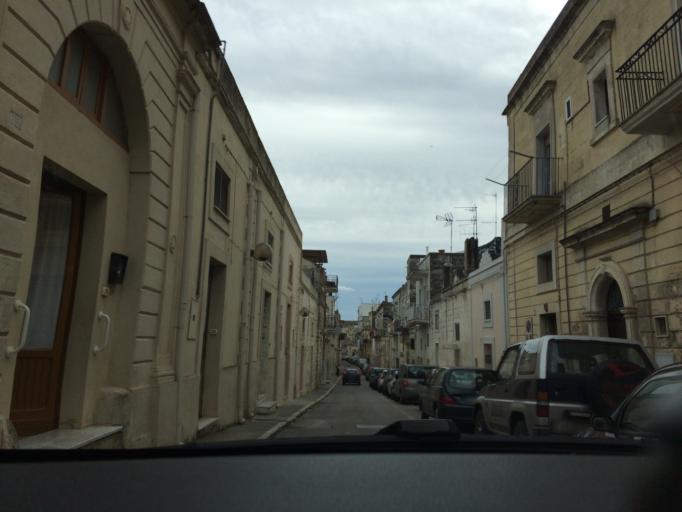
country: IT
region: Basilicate
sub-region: Provincia di Matera
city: Matera
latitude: 40.6724
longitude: 16.6081
